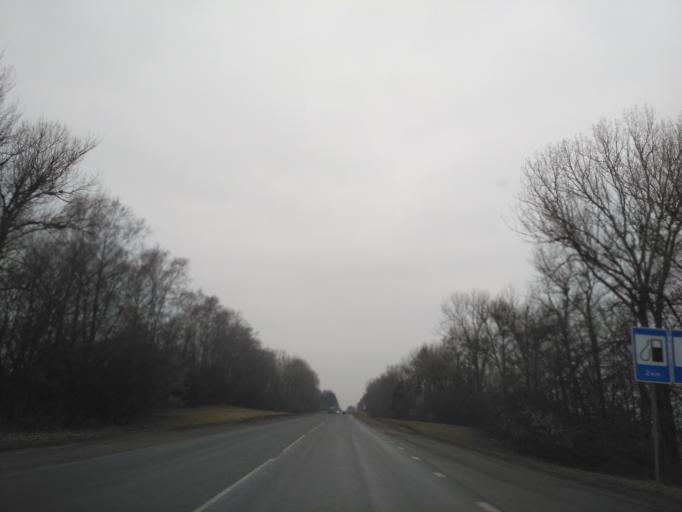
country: BY
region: Brest
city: Baranovichi
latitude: 53.1659
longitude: 26.0250
